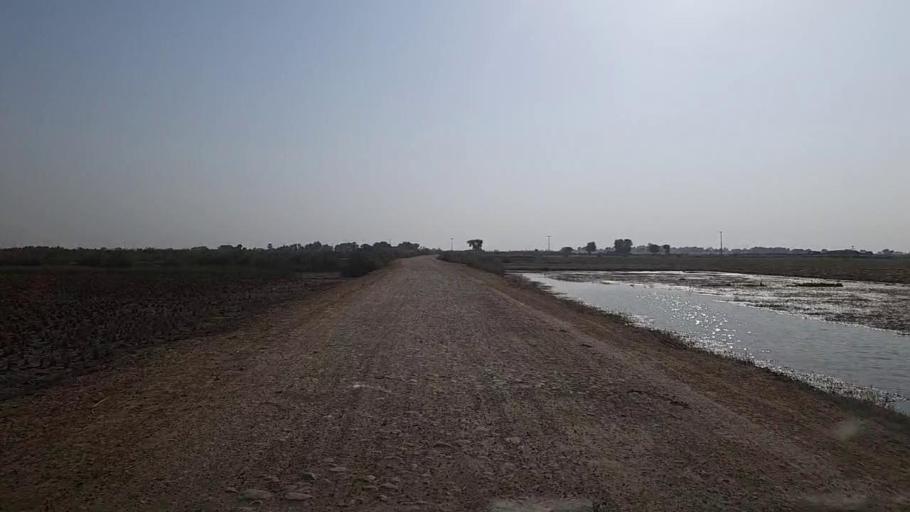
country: PK
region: Sindh
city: Kandhkot
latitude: 28.3856
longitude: 69.3371
